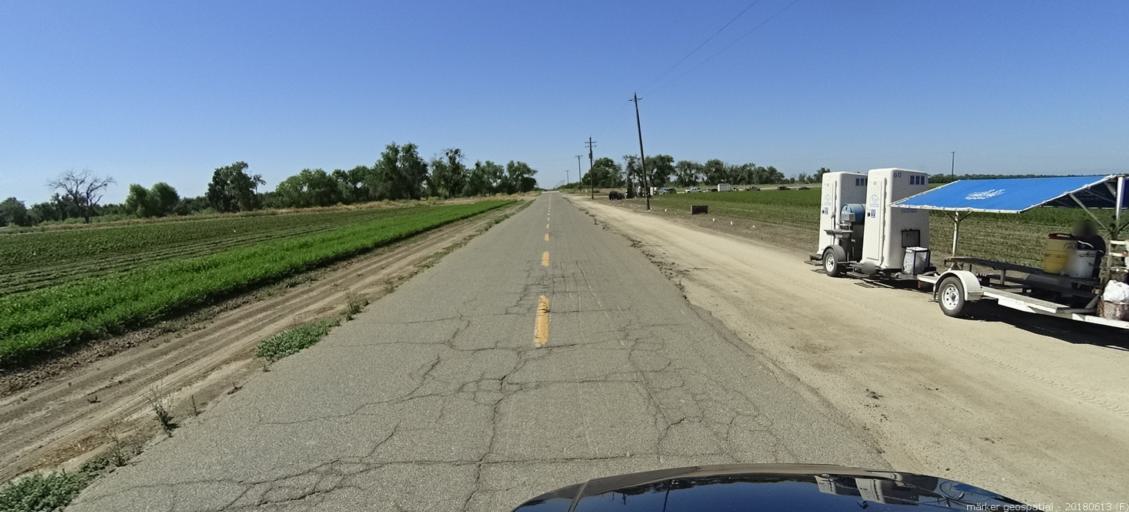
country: US
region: California
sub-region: Madera County
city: Chowchilla
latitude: 37.0669
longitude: -120.4010
